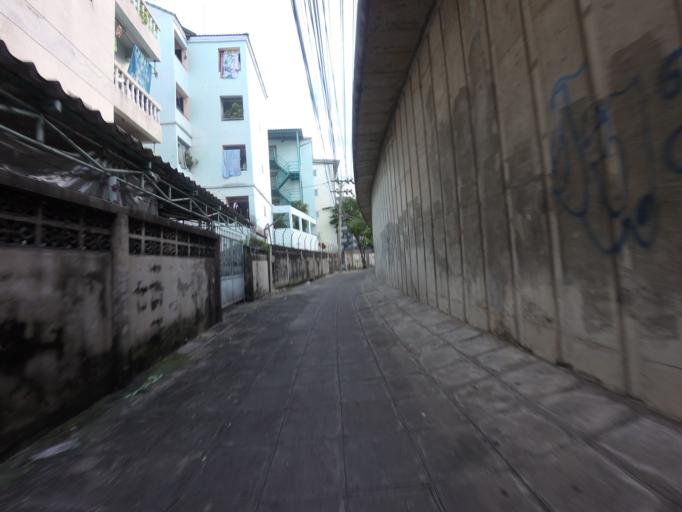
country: TH
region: Bangkok
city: Watthana
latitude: 13.7417
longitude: 100.5912
